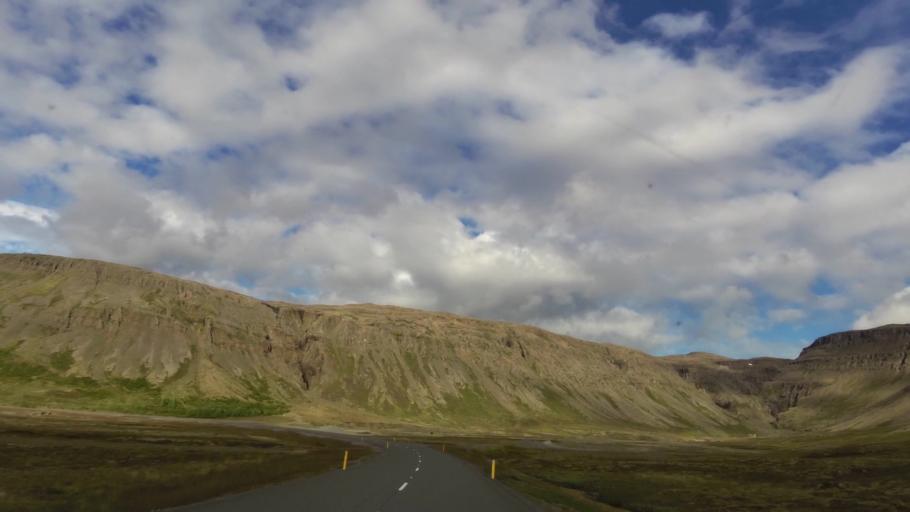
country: IS
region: West
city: Olafsvik
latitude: 65.5135
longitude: -23.8410
